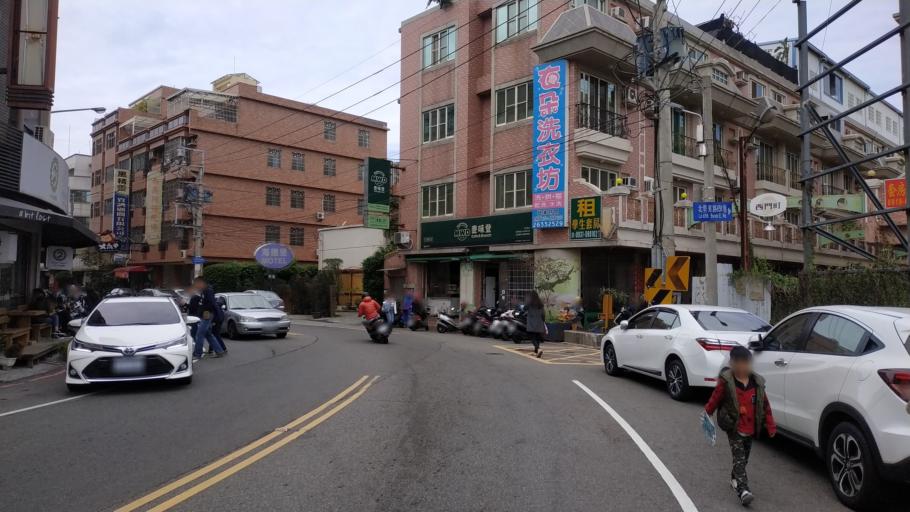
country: TW
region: Taiwan
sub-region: Taichung City
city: Taichung
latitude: 24.2296
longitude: 120.5735
